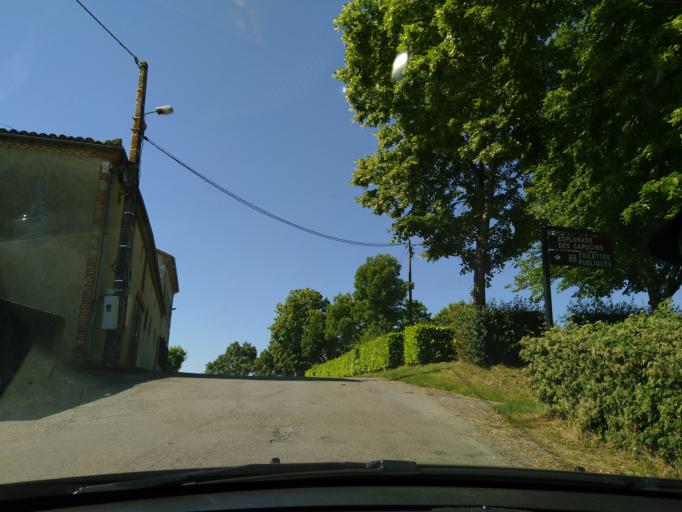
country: FR
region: Midi-Pyrenees
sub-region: Departement du Gers
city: Gimont
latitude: 43.6252
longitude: 0.8740
